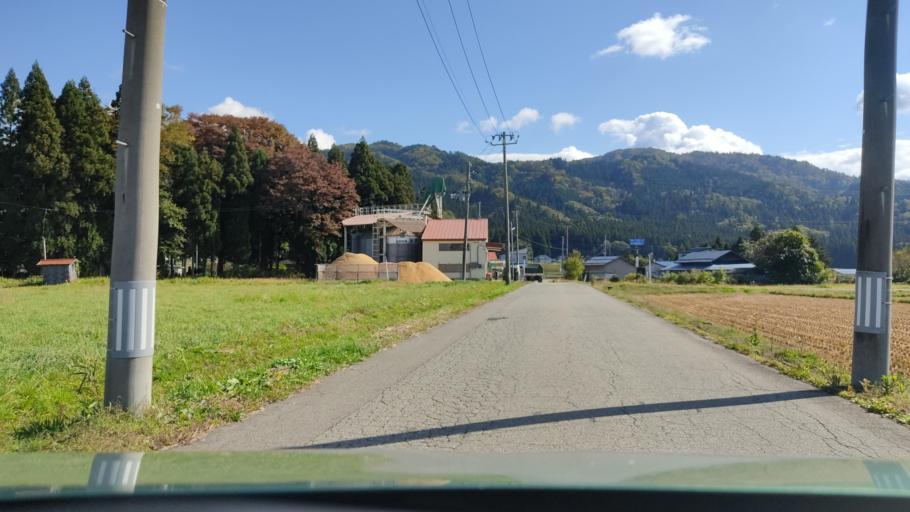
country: JP
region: Akita
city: Yokotemachi
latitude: 39.4034
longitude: 140.5828
